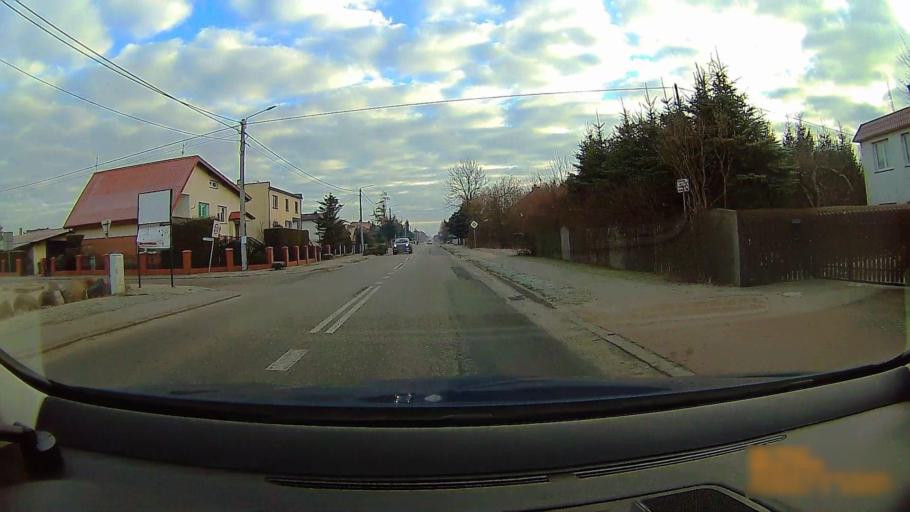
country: PL
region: Greater Poland Voivodeship
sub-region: Powiat koninski
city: Rzgow Pierwszy
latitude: 52.1558
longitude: 18.0546
